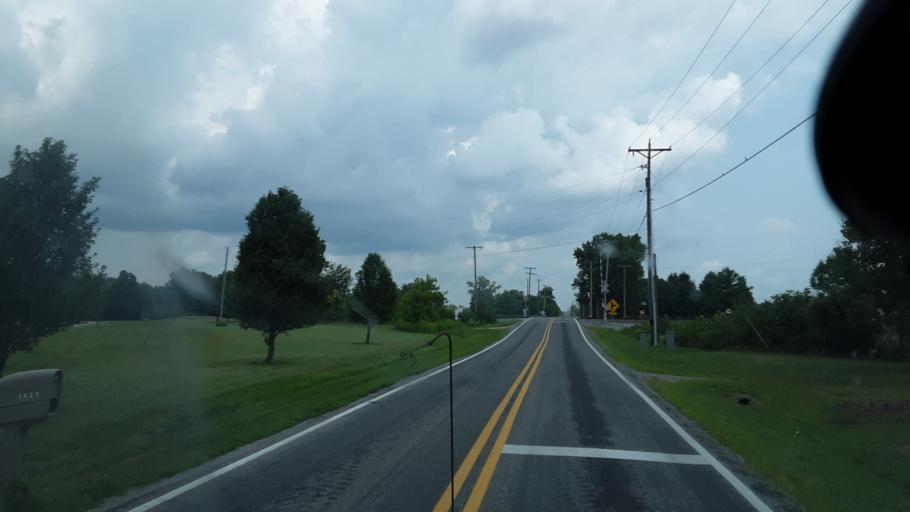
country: US
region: Ohio
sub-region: Delaware County
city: Delaware
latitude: 40.3165
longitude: -83.0503
